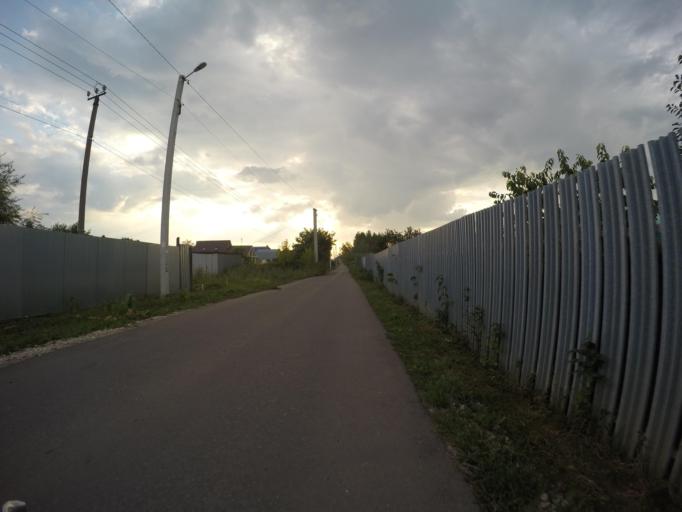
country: RU
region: Moskovskaya
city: Rechitsy
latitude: 55.5912
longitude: 38.5014
